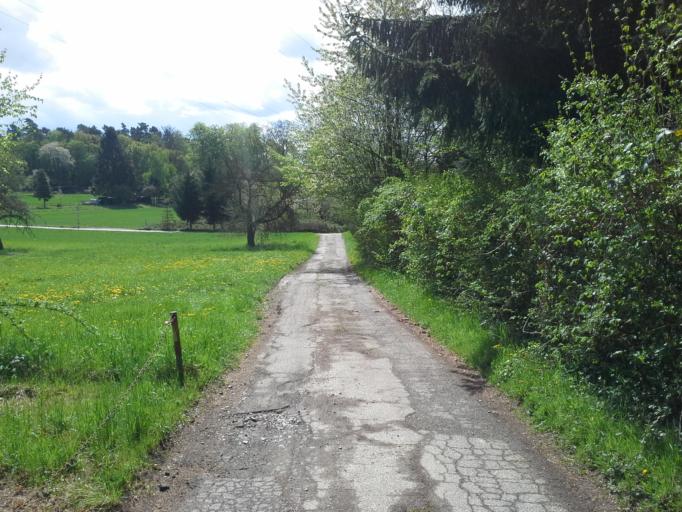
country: DE
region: Baden-Wuerttemberg
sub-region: Karlsruhe Region
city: Ispringen
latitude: 48.9001
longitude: 8.6463
